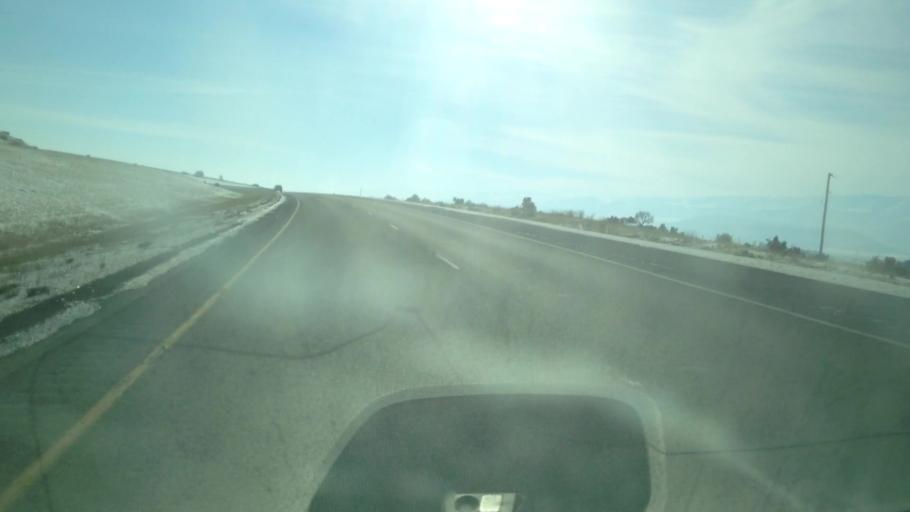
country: US
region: Idaho
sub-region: Oneida County
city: Malad City
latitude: 42.1360
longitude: -112.2204
